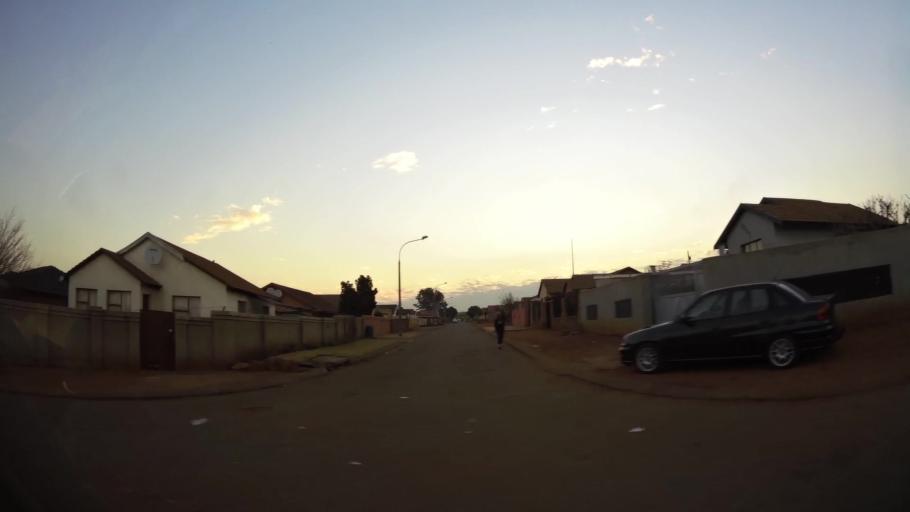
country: ZA
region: Gauteng
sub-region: West Rand District Municipality
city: Randfontein
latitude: -26.2110
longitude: 27.7187
